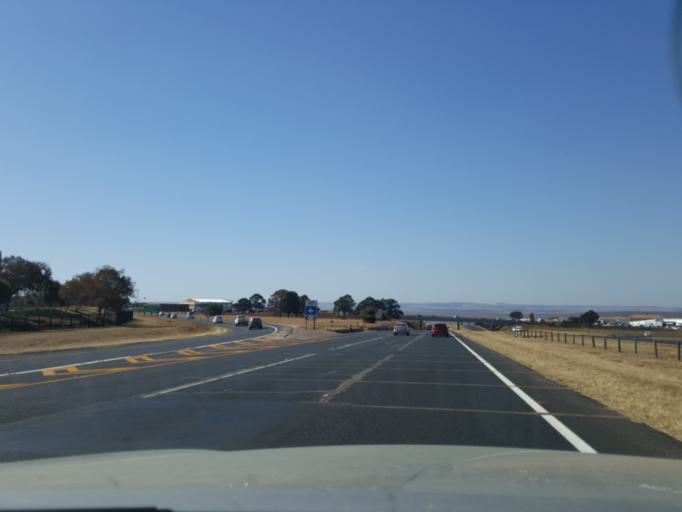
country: ZA
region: Mpumalanga
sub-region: Nkangala District Municipality
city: Witbank
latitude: -25.8898
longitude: 29.2678
